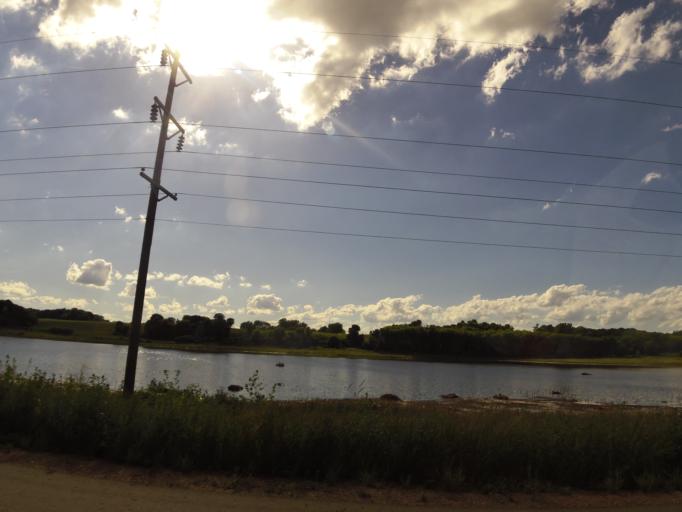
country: US
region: Minnesota
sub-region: Carver County
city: Waconia
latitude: 44.8710
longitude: -93.8134
